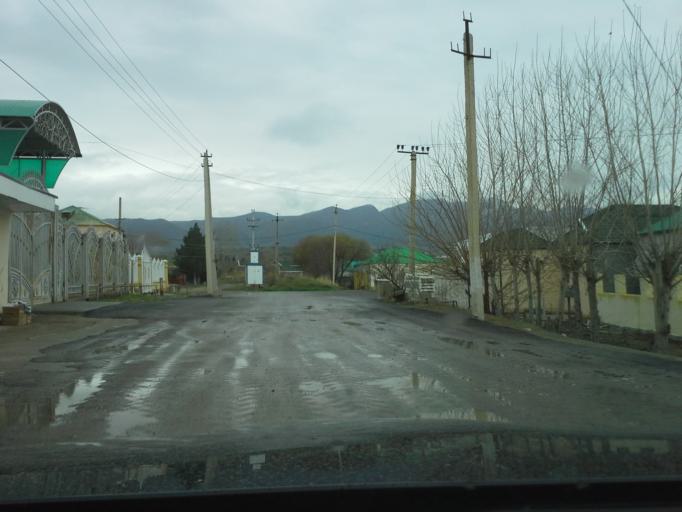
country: TM
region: Ahal
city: Abadan
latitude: 37.9610
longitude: 58.2283
